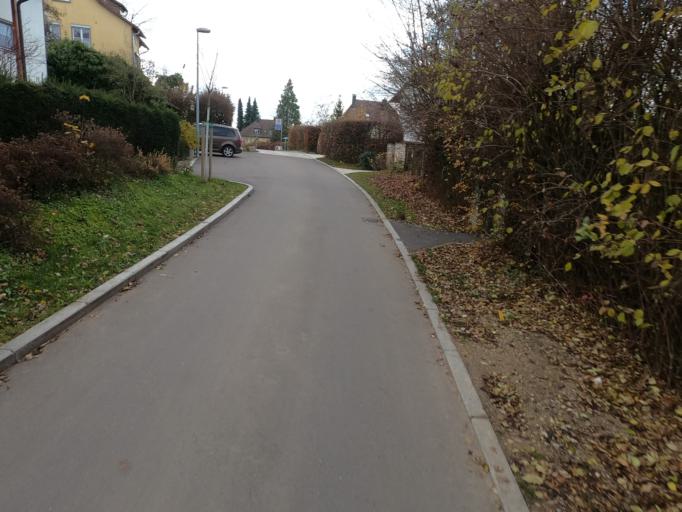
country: DE
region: Baden-Wuerttemberg
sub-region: Regierungsbezirk Stuttgart
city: Goeppingen
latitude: 48.6965
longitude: 9.6384
